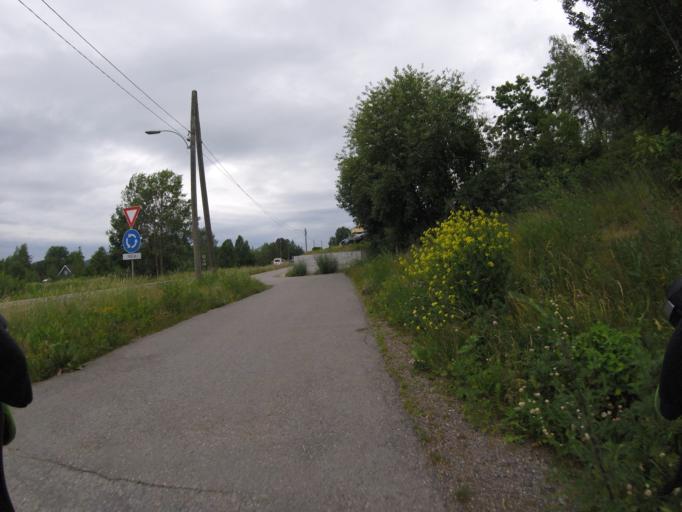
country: NO
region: Akershus
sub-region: Skedsmo
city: Lillestrom
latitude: 59.9754
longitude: 11.0283
